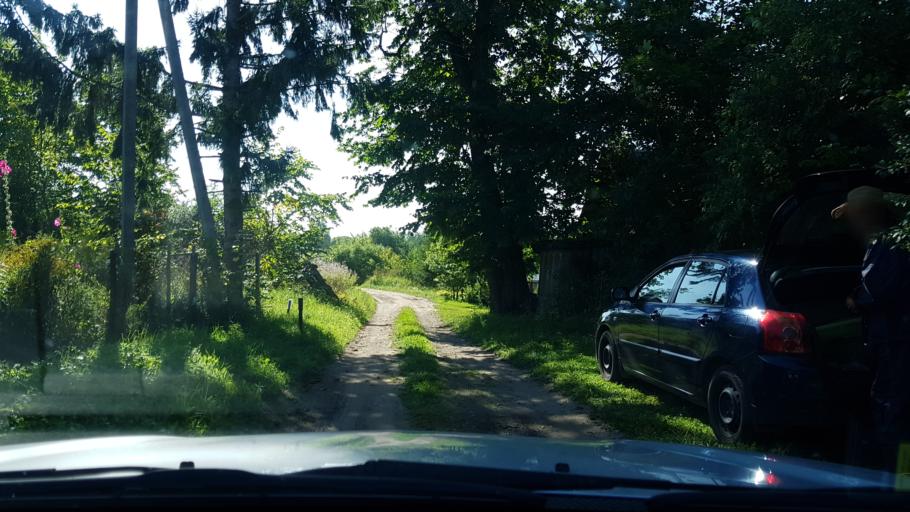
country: EE
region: Ida-Virumaa
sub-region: Sillamaee linn
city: Sillamae
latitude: 59.3254
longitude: 27.7760
